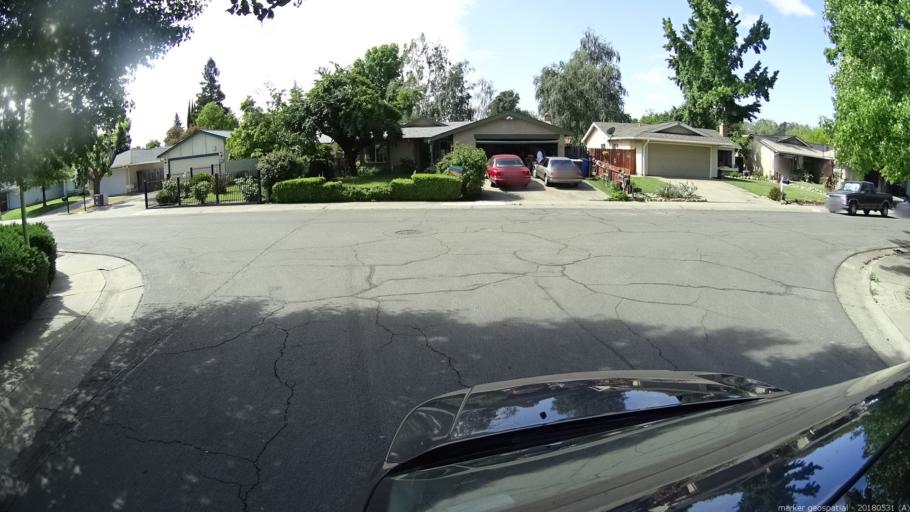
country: US
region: California
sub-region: Sacramento County
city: Sacramento
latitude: 38.6182
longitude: -121.5043
